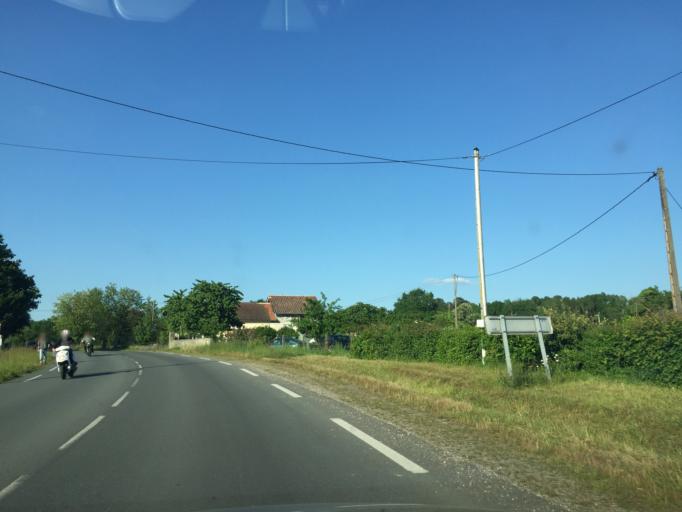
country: FR
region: Aquitaine
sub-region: Departement de la Dordogne
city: La Roche-Chalais
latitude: 45.1640
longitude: 0.0095
